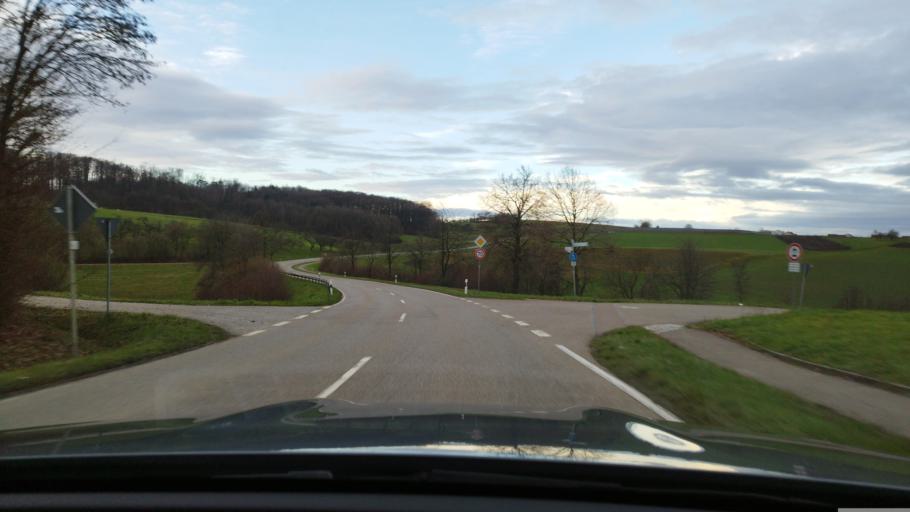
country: DE
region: Baden-Wuerttemberg
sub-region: Regierungsbezirk Stuttgart
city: Burgstetten
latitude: 48.9251
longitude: 9.3853
